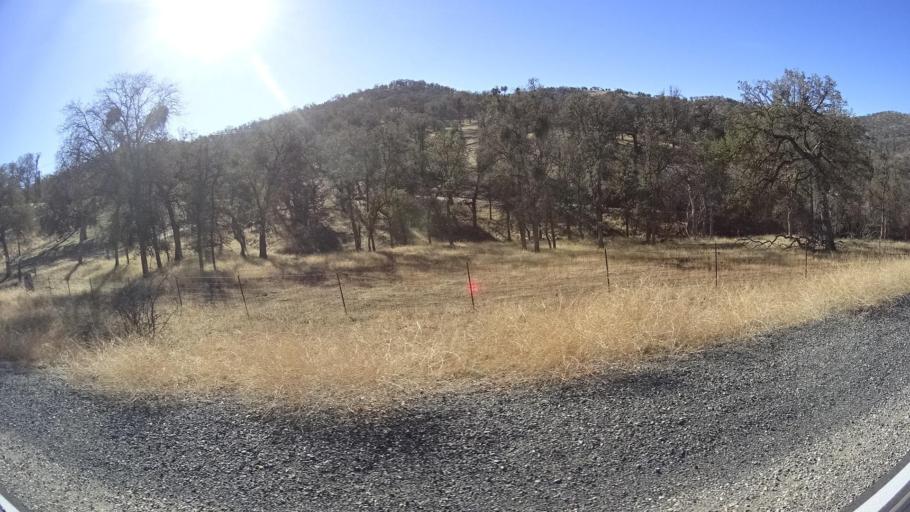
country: US
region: California
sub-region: Kern County
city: Alta Sierra
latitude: 35.7059
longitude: -118.7632
